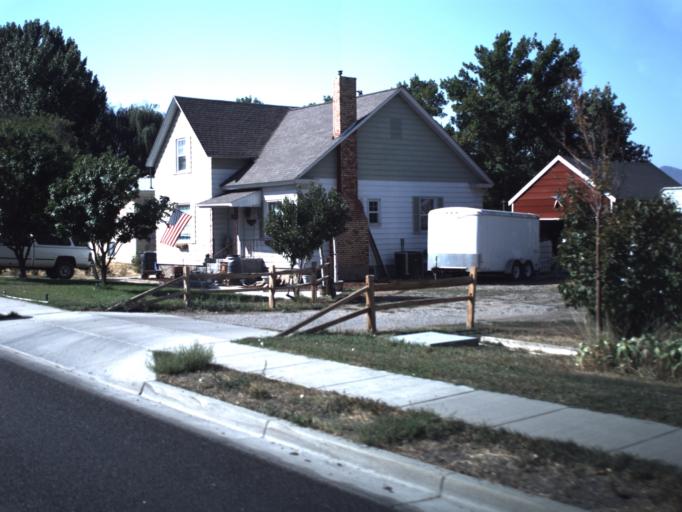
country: US
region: Utah
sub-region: Cache County
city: Nibley
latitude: 41.6728
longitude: -111.8335
